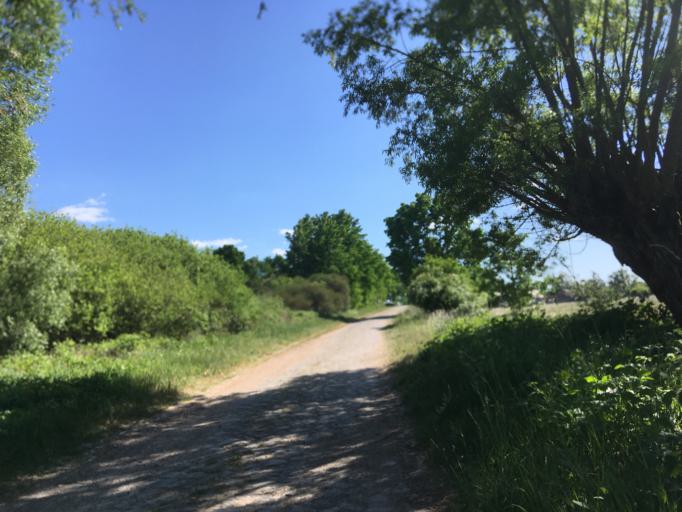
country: DE
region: Brandenburg
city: Althuttendorf
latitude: 52.9720
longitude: 13.8146
